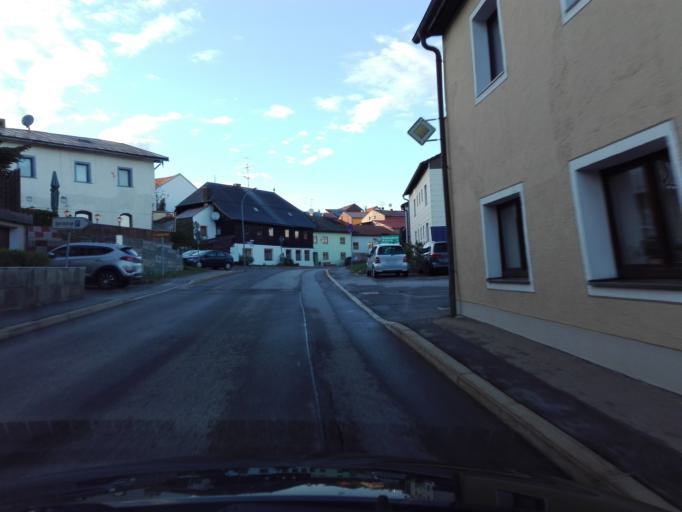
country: DE
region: Bavaria
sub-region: Lower Bavaria
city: Wegscheid
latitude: 48.5995
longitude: 13.7853
